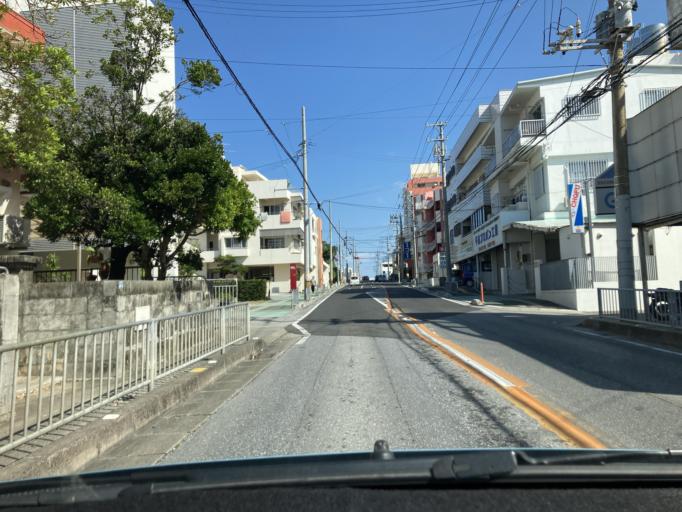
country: JP
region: Okinawa
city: Tomigusuku
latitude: 26.1874
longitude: 127.6674
